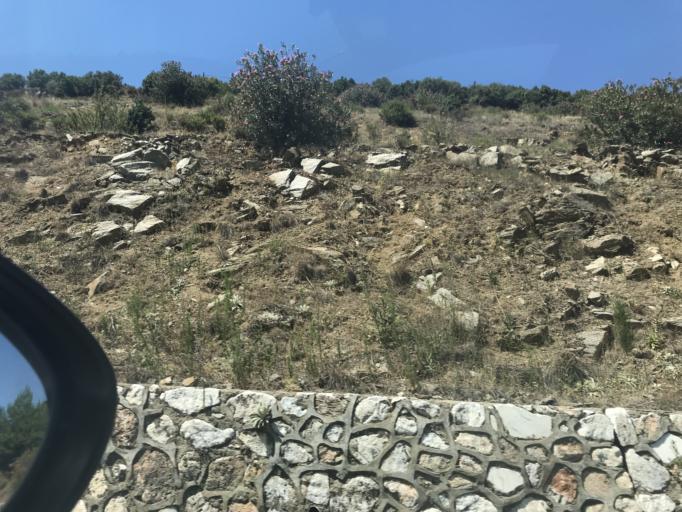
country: TR
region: Aydin
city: Akcaova
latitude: 37.5064
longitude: 28.1023
